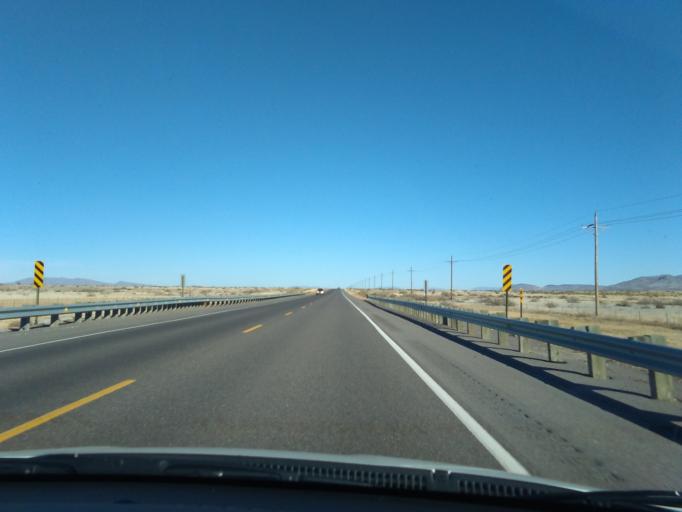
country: US
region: New Mexico
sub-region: Dona Ana County
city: Hatch
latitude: 32.5919
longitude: -107.3522
